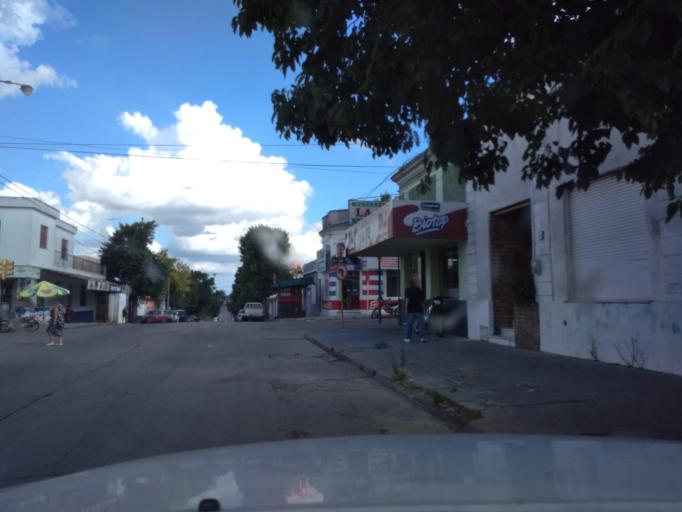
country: UY
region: Florida
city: Florida
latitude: -34.0950
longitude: -56.2121
